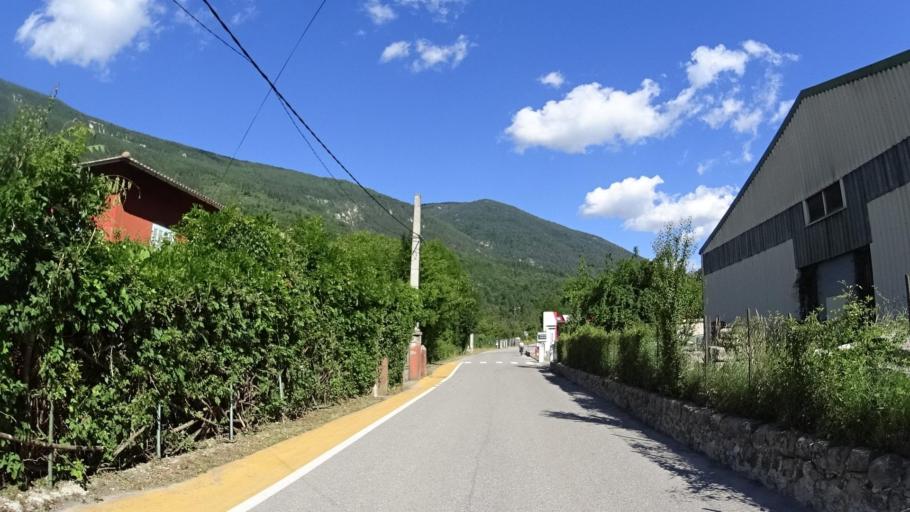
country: FR
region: Provence-Alpes-Cote d'Azur
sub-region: Departement des Alpes-de-Haute-Provence
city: Annot
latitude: 43.9728
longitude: 6.6565
